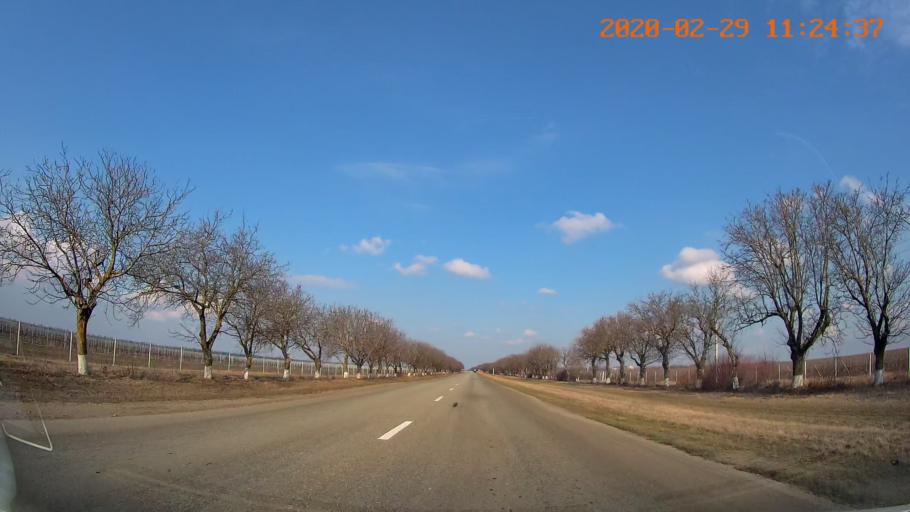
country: MD
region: Telenesti
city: Cocieri
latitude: 47.4265
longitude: 29.1538
